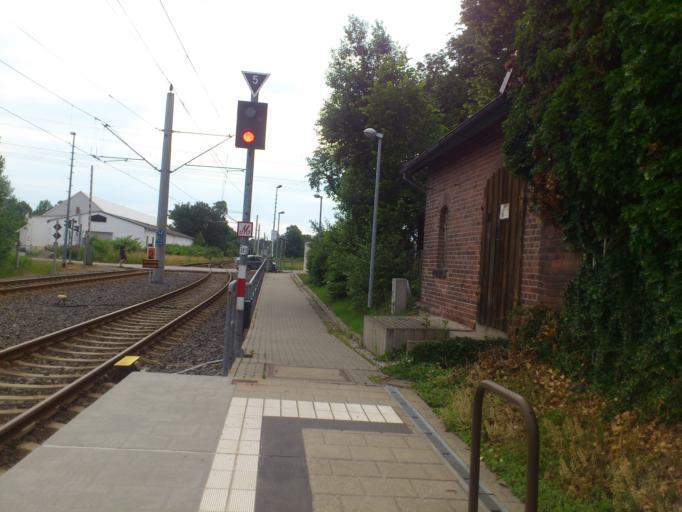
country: DE
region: Saxony
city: Neukirchen
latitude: 50.7710
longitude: 12.8933
